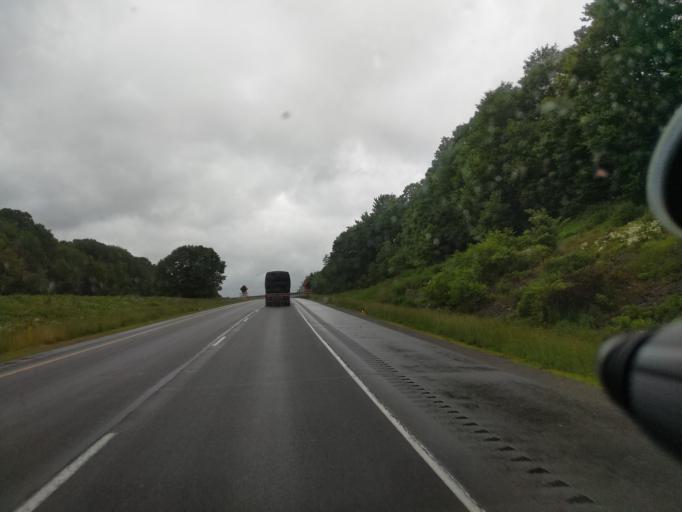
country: US
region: Pennsylvania
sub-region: Clearfield County
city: Treasure Lake
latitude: 41.1230
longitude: -78.6832
